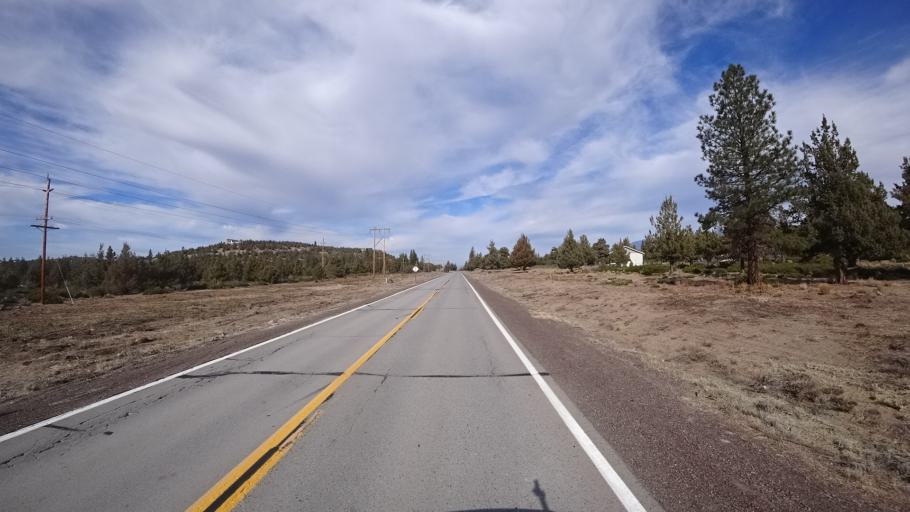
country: US
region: California
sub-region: Siskiyou County
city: Weed
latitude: 41.5305
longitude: -122.3647
